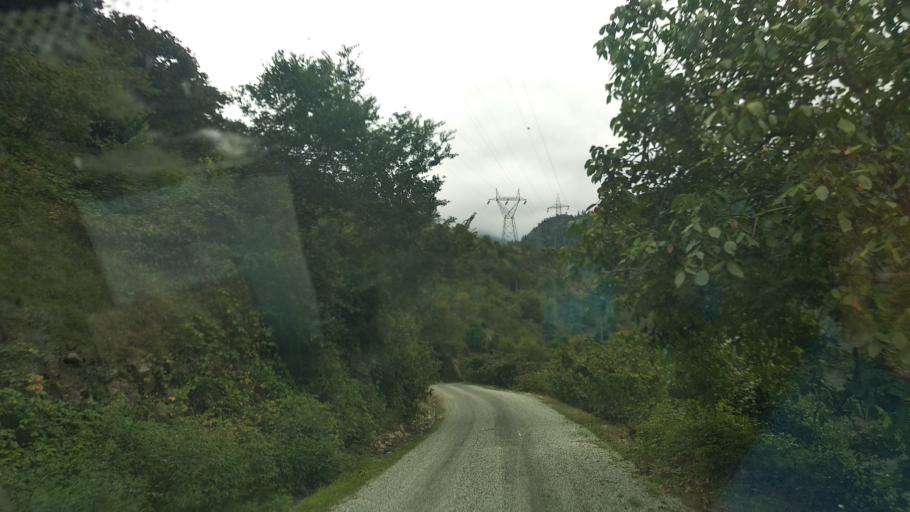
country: TR
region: Giresun
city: Dogankent
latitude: 40.7423
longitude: 38.9860
